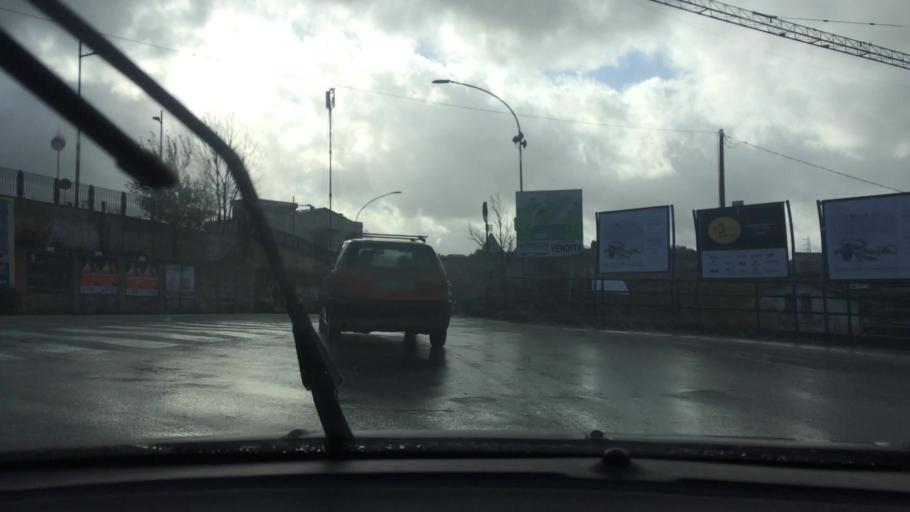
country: IT
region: Basilicate
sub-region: Provincia di Potenza
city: Potenza
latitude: 40.6389
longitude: 15.7872
